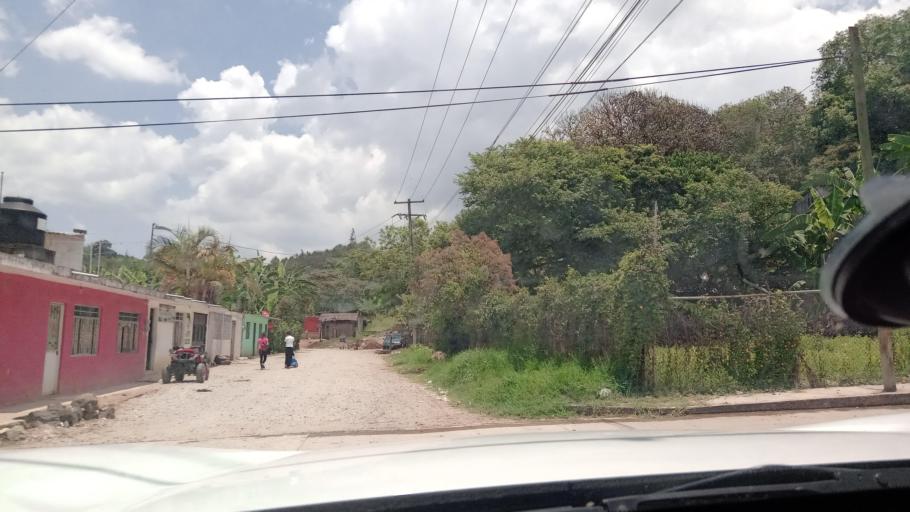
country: MX
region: Veracruz
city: Coatepec
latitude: 19.4306
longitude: -96.9781
